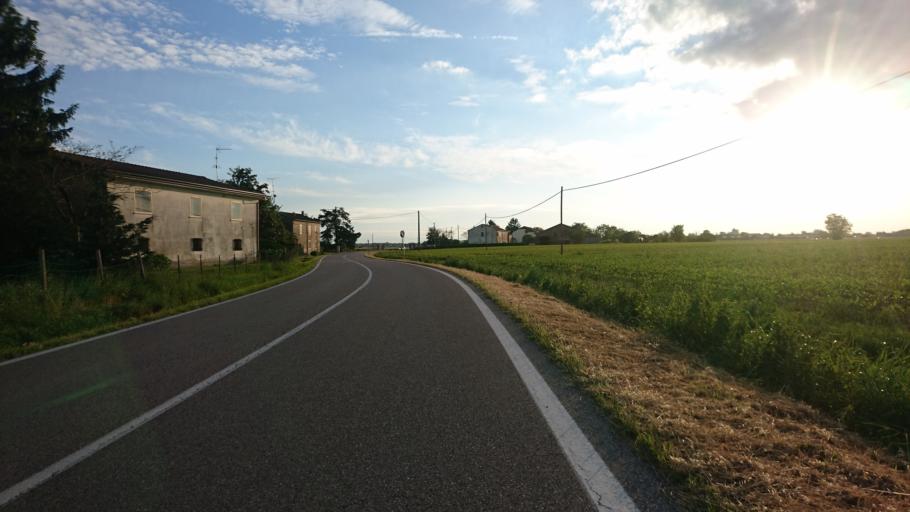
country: IT
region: Veneto
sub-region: Provincia di Rovigo
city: Castelmassa
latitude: 45.0179
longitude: 11.3382
